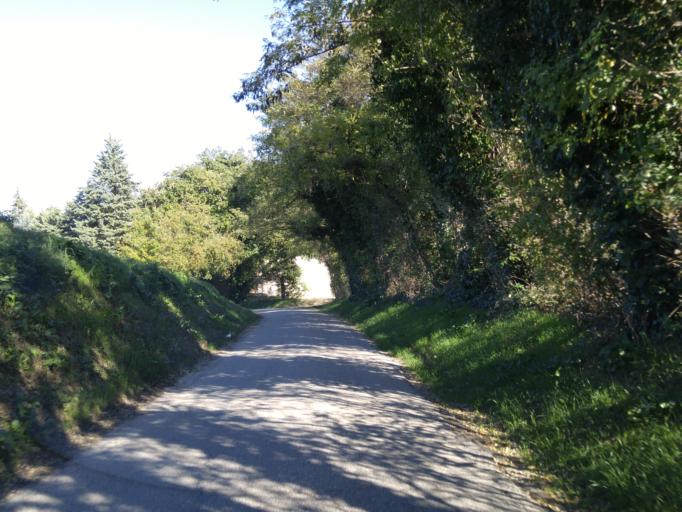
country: IT
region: The Marches
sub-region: Provincia di Pesaro e Urbino
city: Tavernelle
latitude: 43.7107
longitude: 12.8821
